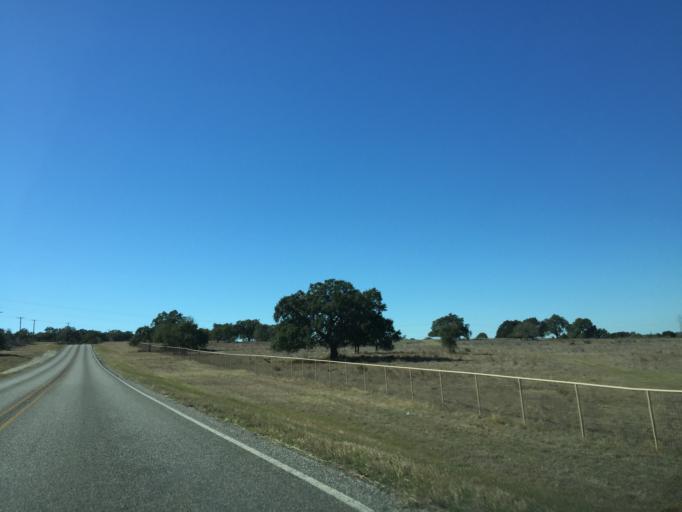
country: US
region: Texas
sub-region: Comal County
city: Canyon Lake
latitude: 29.7686
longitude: -98.2989
